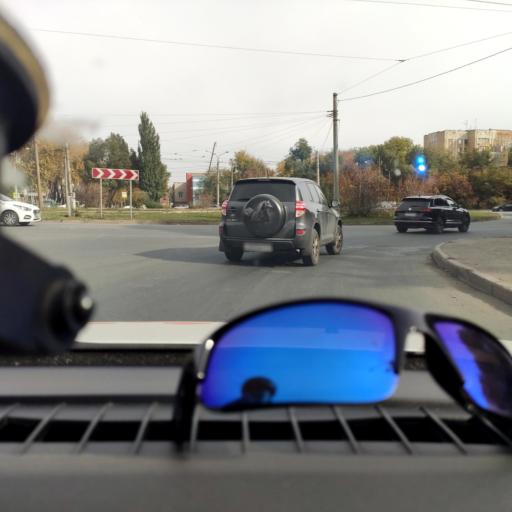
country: RU
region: Samara
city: Samara
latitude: 53.2032
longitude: 50.2384
